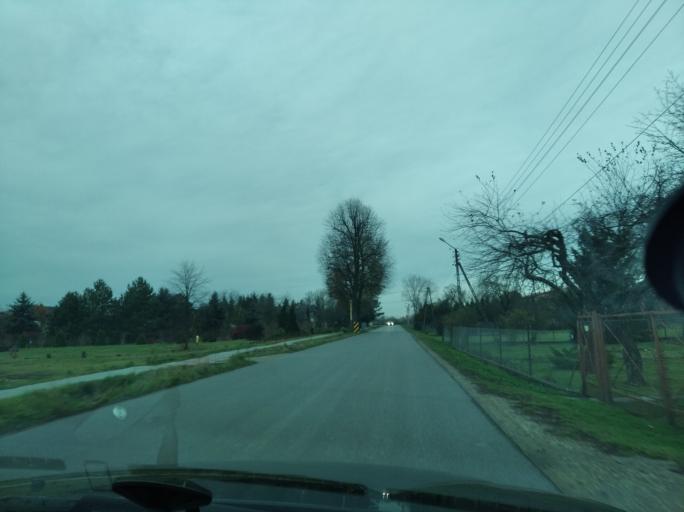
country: PL
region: Subcarpathian Voivodeship
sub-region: Powiat lancucki
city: Czarna
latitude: 50.0997
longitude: 22.2046
